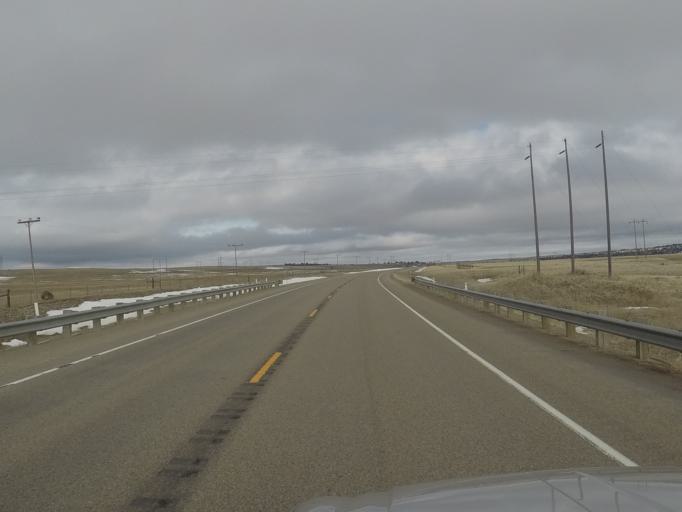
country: US
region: Montana
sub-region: Golden Valley County
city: Ryegate
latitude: 46.3287
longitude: -109.4711
